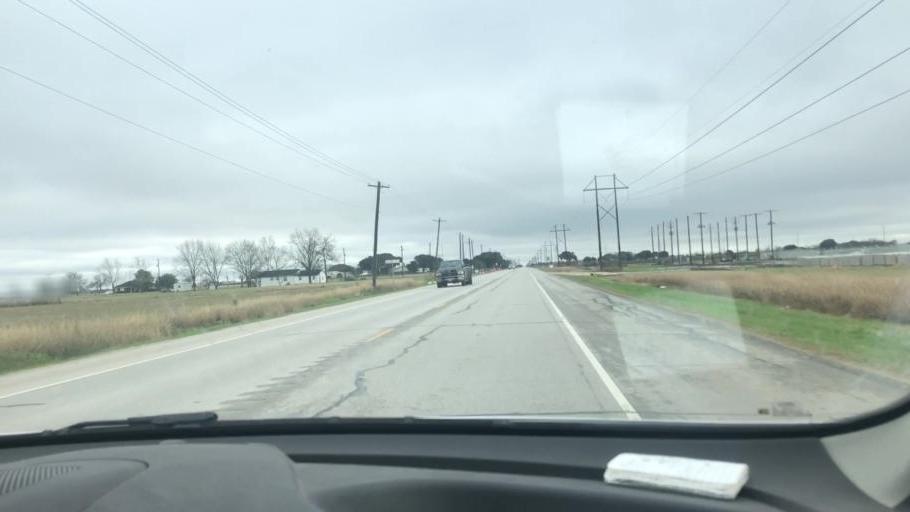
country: US
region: Texas
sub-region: Wharton County
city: Boling
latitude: 29.2076
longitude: -96.0247
